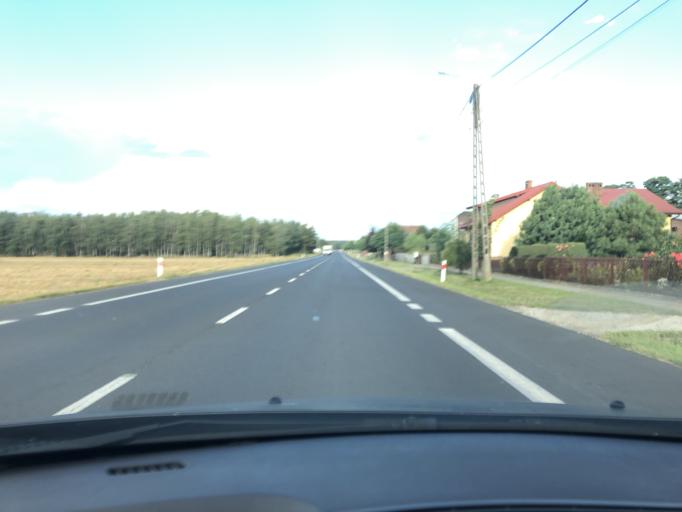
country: PL
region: Lodz Voivodeship
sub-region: Powiat wieruszowski
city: Galewice
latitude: 51.3040
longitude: 18.2500
